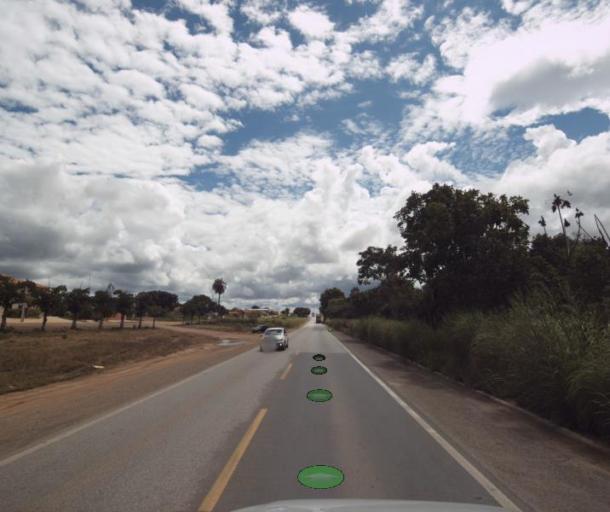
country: BR
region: Goias
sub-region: Uruacu
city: Uruacu
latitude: -14.3206
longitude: -49.1514
